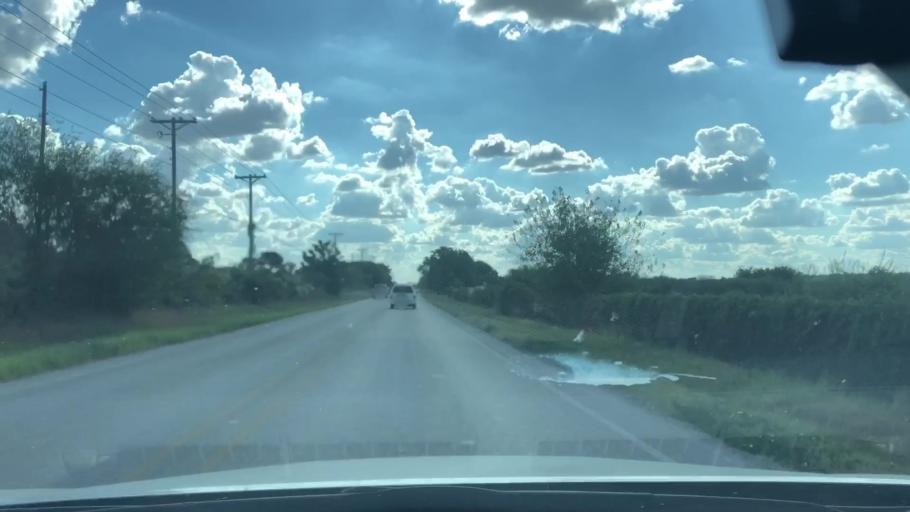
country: US
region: Texas
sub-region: Guadalupe County
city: Northcliff
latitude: 29.6610
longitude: -98.1924
